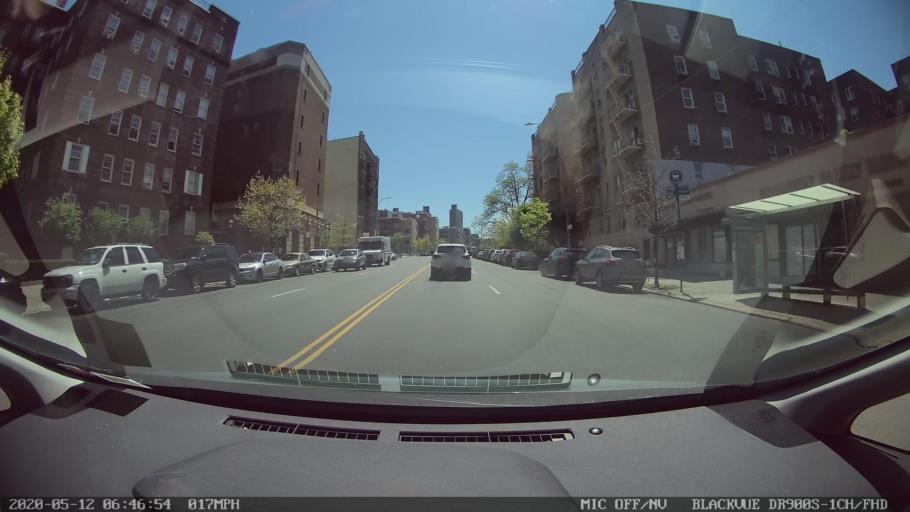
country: US
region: New York
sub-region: New York County
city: Inwood
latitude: 40.8551
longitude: -73.9334
